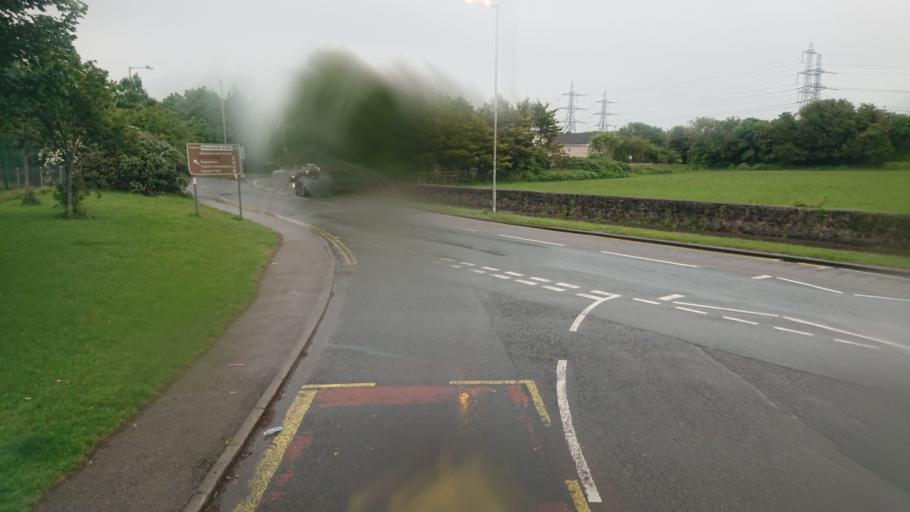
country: GB
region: England
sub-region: Lancashire
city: Morecambe
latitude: 54.0356
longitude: -2.8973
